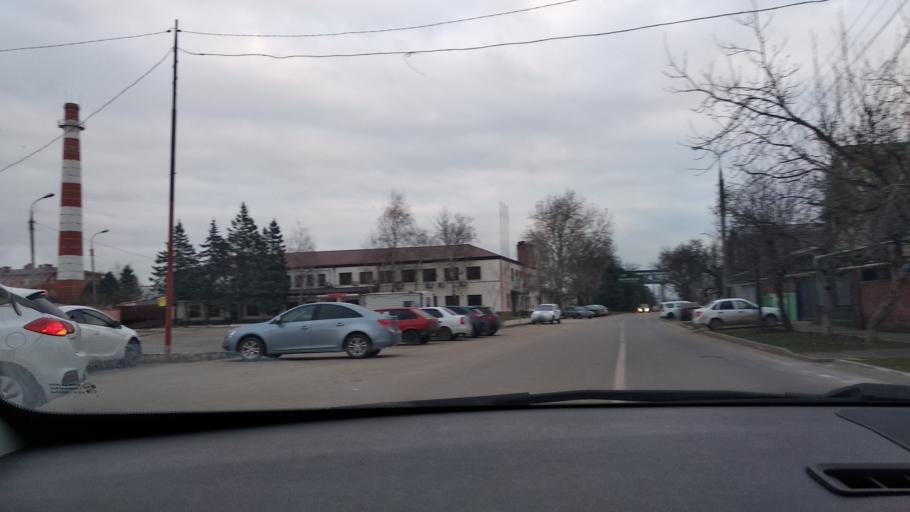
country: RU
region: Krasnodarskiy
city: Krasnodar
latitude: 45.0001
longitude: 39.0249
